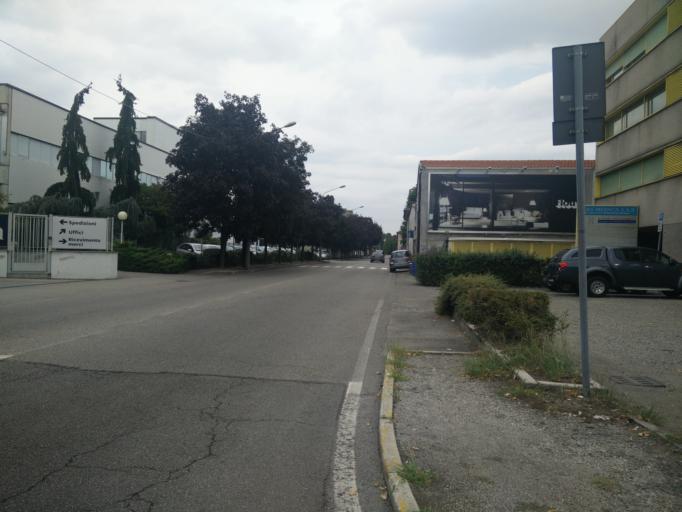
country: IT
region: Lombardy
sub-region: Provincia di Monza e Brianza
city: Meda
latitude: 45.6587
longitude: 9.1581
